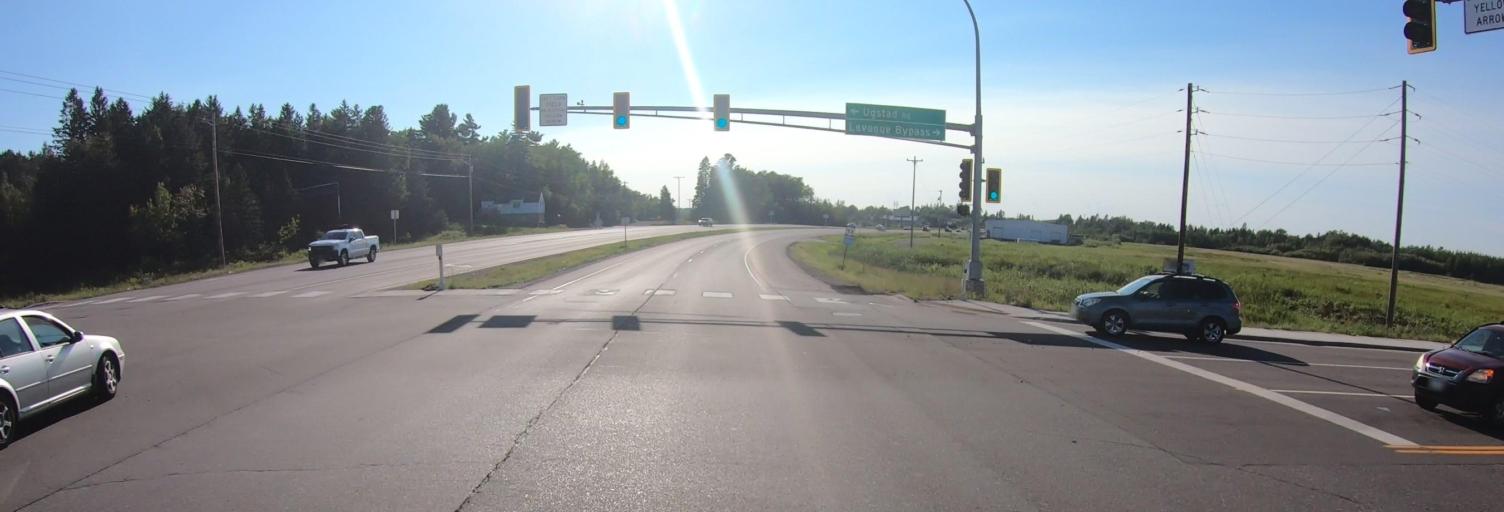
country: US
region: Minnesota
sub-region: Saint Louis County
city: Hermantown
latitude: 46.8367
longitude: -92.2385
